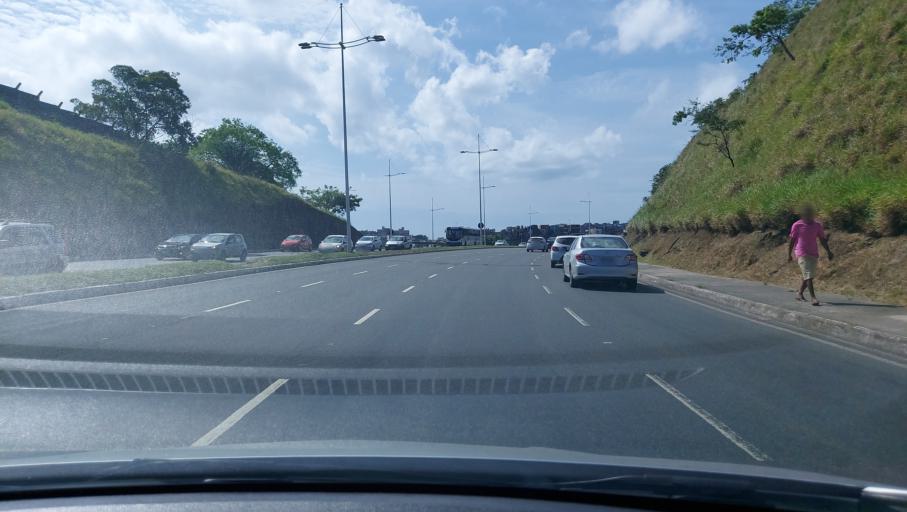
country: BR
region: Bahia
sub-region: Salvador
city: Salvador
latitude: -12.9537
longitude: -38.4731
